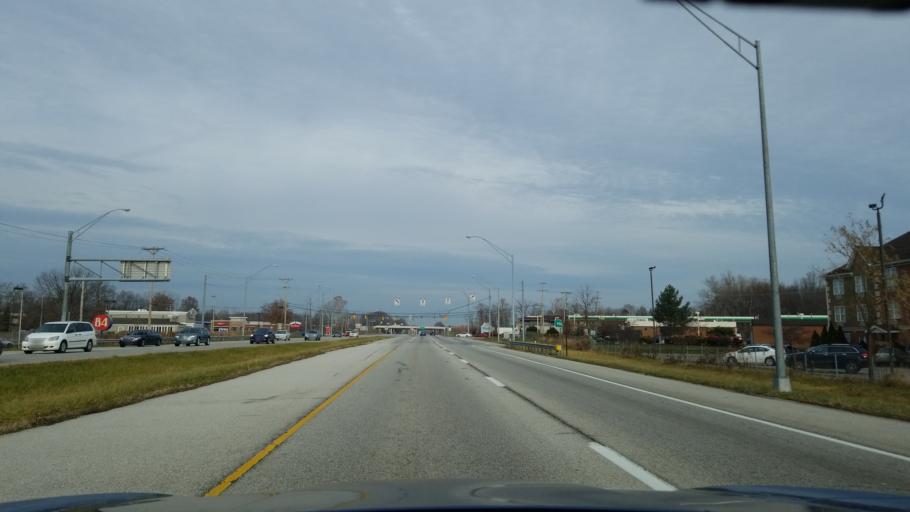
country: US
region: Ohio
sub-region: Summit County
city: Macedonia
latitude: 41.2974
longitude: -81.5138
